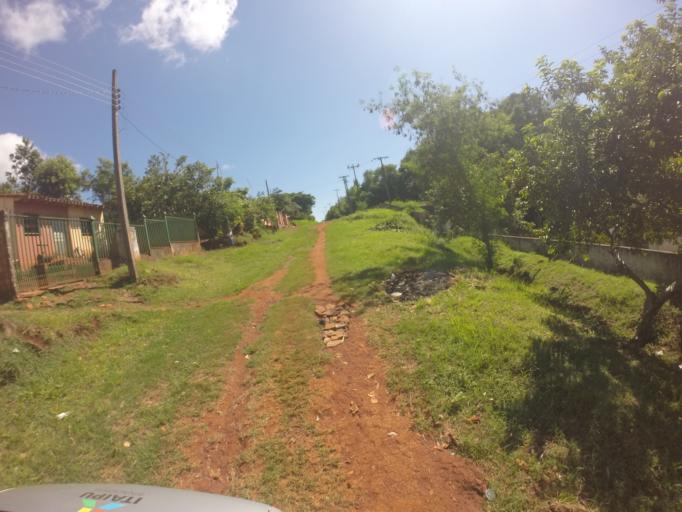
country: PY
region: Alto Parana
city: Ciudad del Este
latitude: -25.4429
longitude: -54.6420
